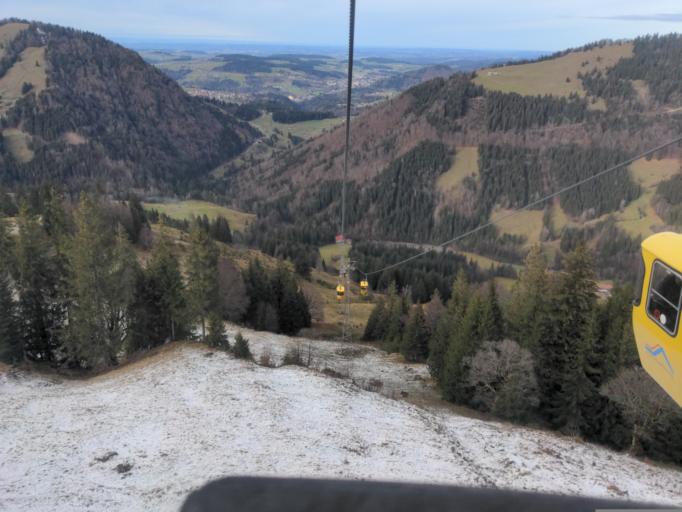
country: DE
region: Bavaria
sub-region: Swabia
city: Balderschwang
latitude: 47.5006
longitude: 10.0656
